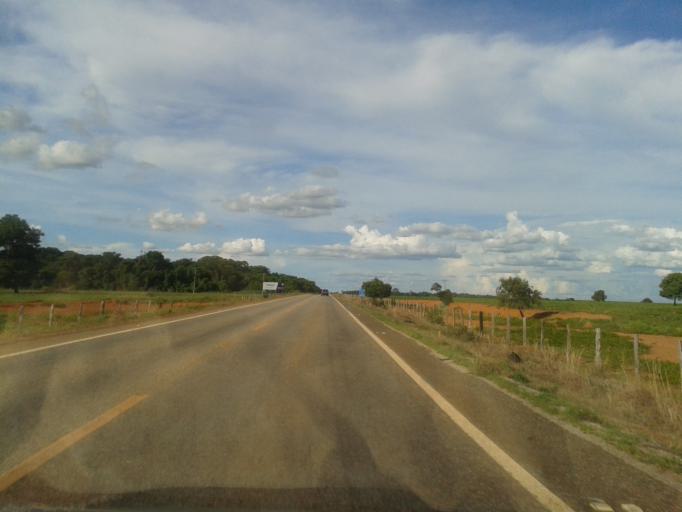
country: BR
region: Goias
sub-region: Mozarlandia
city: Mozarlandia
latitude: -14.3339
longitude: -50.4154
